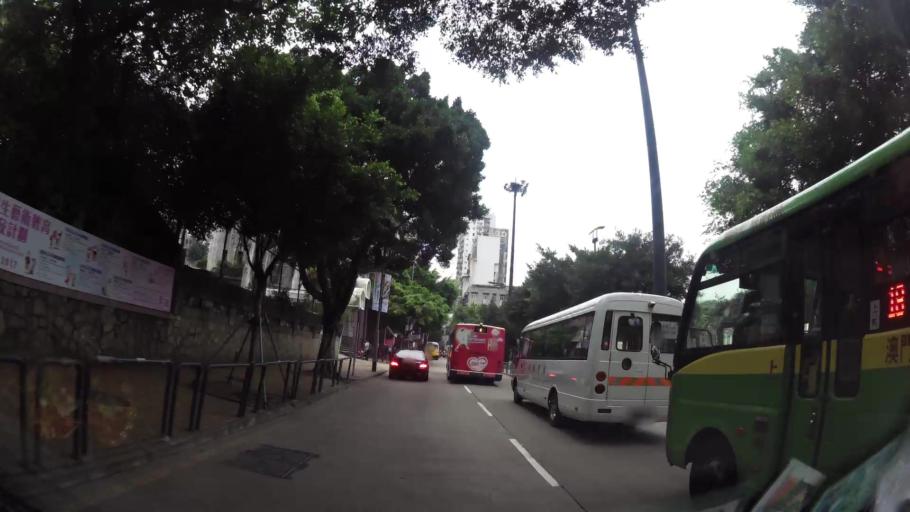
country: MO
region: Macau
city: Macau
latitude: 22.1982
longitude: 113.5477
